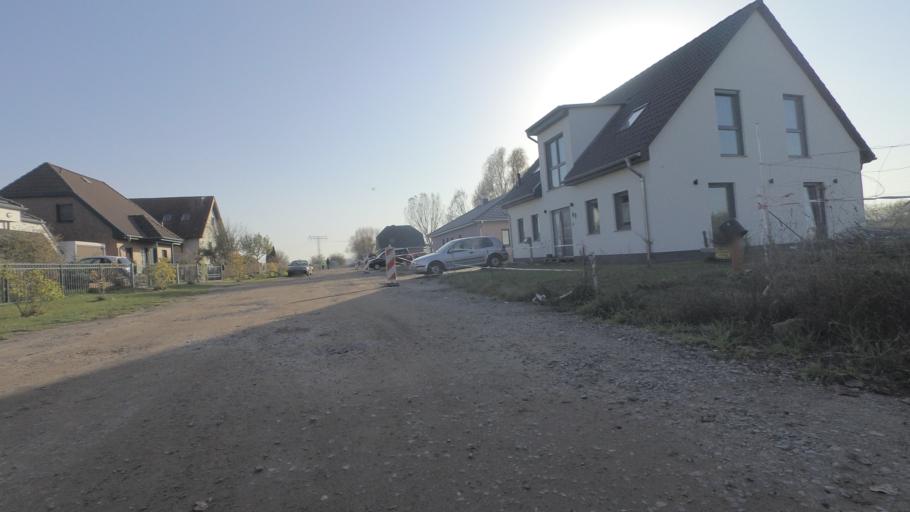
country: DE
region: Brandenburg
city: Zossen
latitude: 52.2212
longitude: 13.4214
